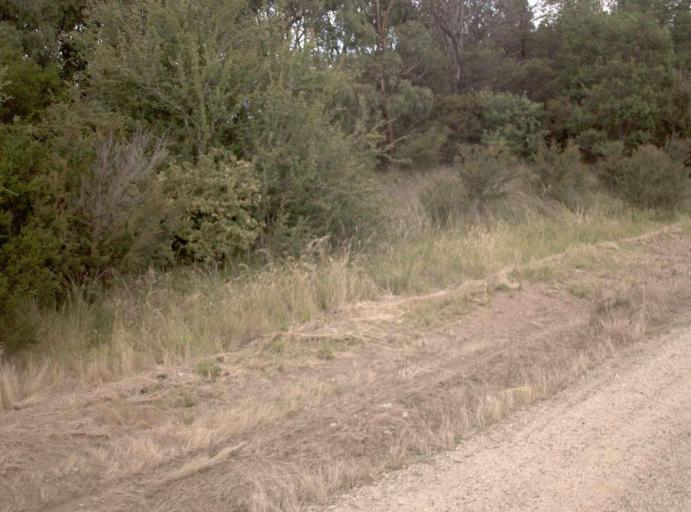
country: AU
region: Victoria
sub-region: Wellington
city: Sale
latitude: -38.1780
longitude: 147.0893
